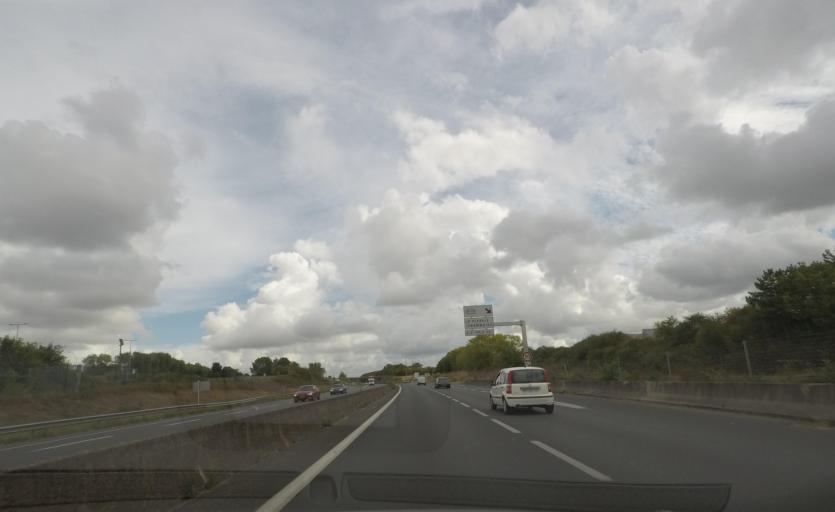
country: FR
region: Pays de la Loire
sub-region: Departement de Maine-et-Loire
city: Trelaze
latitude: 47.4795
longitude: -0.5001
